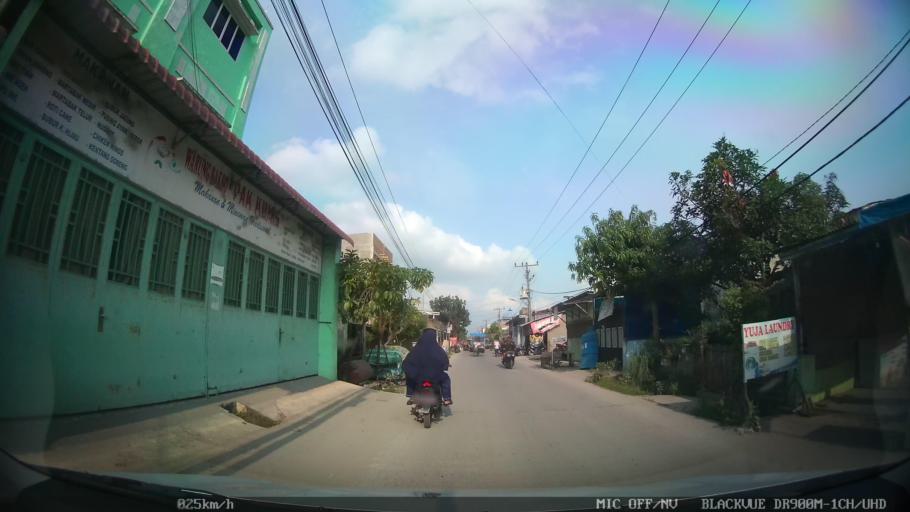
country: ID
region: North Sumatra
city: Medan
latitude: 3.5852
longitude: 98.7519
